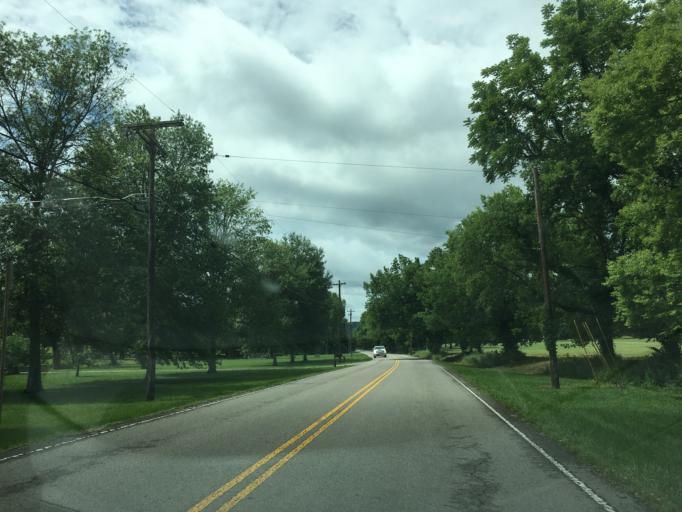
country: US
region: Tennessee
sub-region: Davidson County
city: Forest Hills
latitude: 36.0584
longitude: -86.8749
